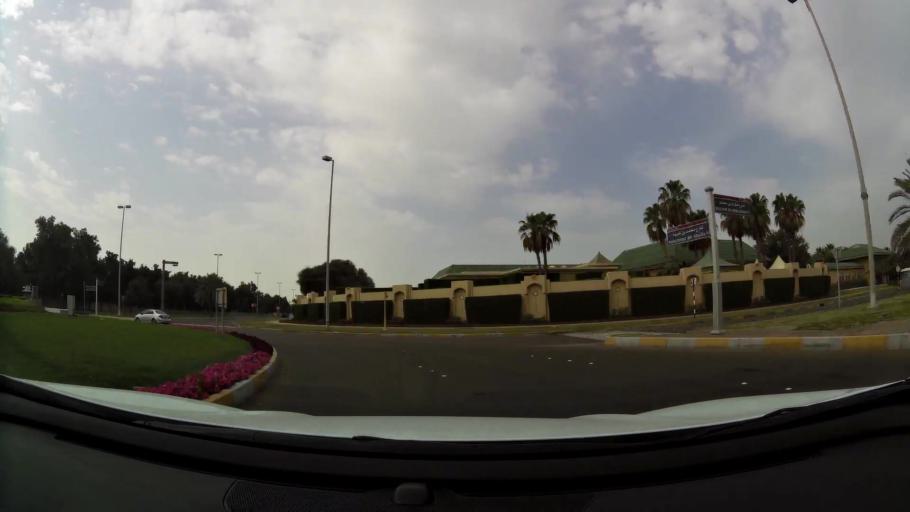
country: AE
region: Abu Dhabi
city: Abu Dhabi
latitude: 24.4503
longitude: 54.3724
